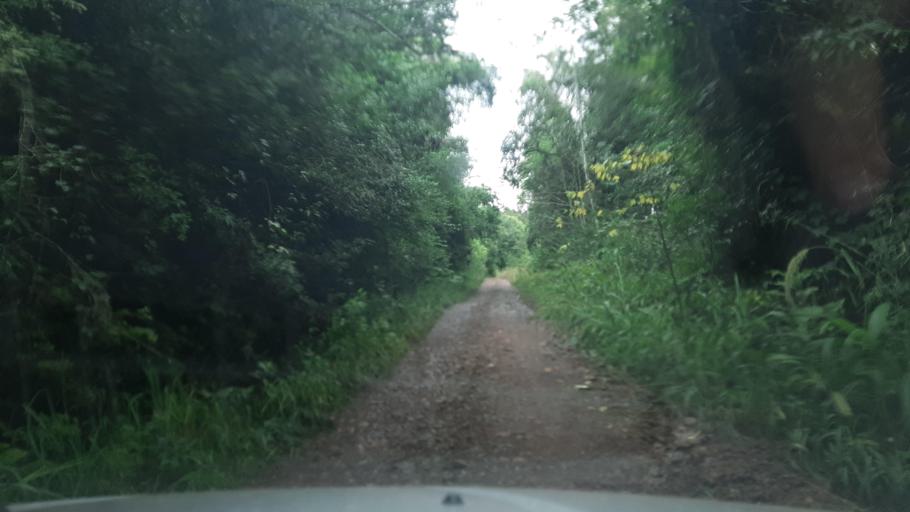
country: BR
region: Parana
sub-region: Ampere
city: Ampere
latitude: -26.0495
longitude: -53.5219
